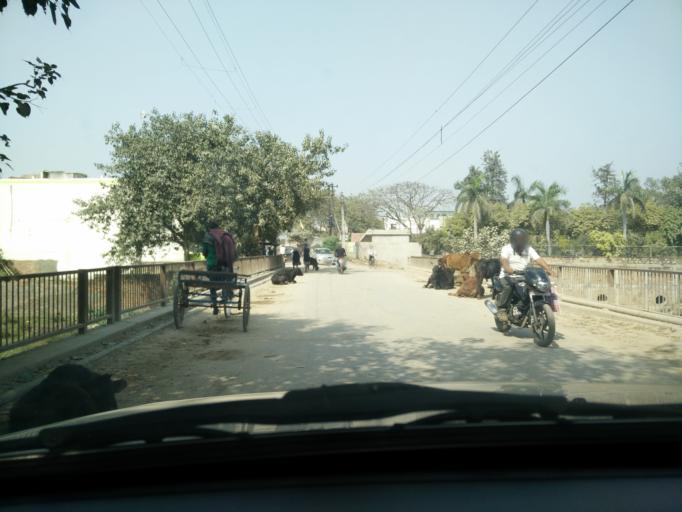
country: IN
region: Uttar Pradesh
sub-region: Varanasi
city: Ramnagar
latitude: 25.2672
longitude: 83.0161
